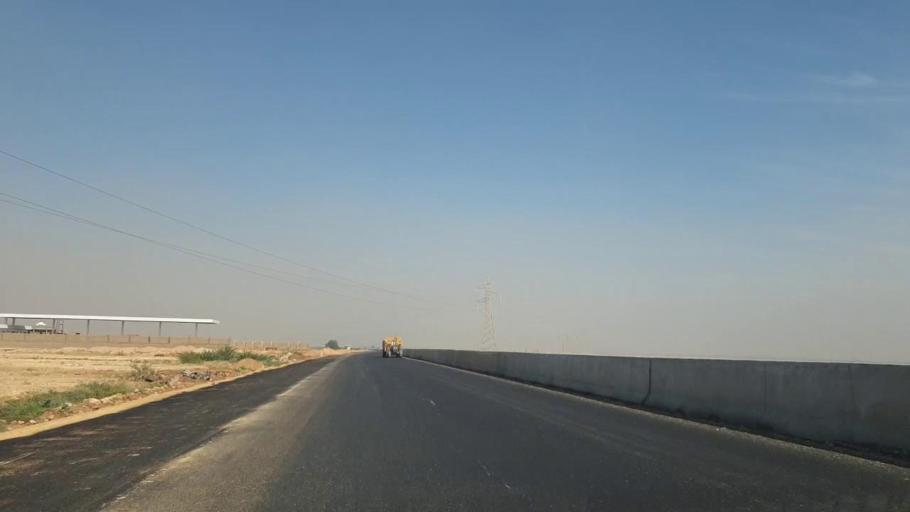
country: PK
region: Sindh
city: Jamshoro
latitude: 25.5340
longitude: 68.2835
